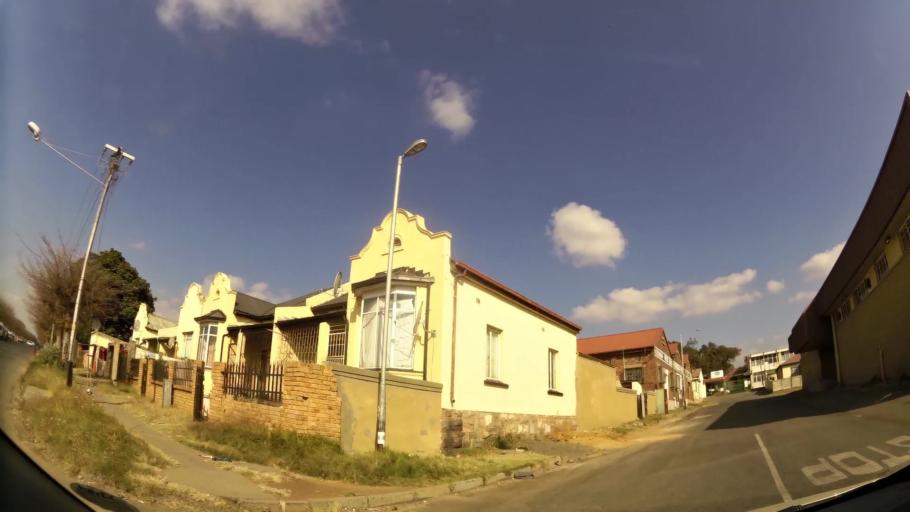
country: ZA
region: Gauteng
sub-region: West Rand District Municipality
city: Krugersdorp
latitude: -26.1069
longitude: 27.7722
